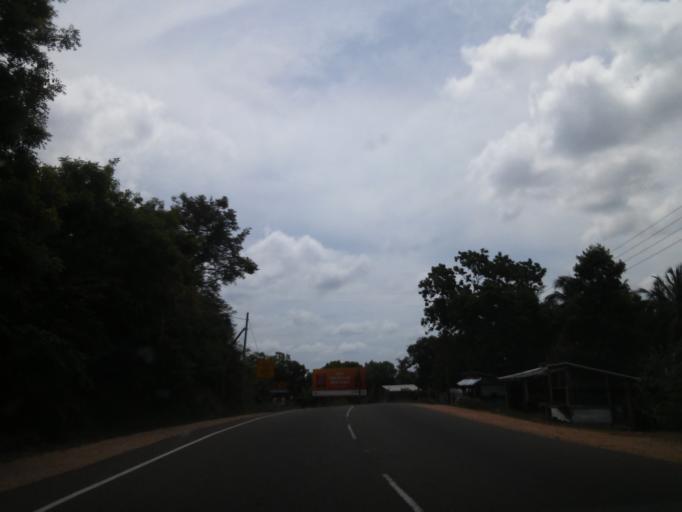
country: LK
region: Eastern Province
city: Trincomalee
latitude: 8.3495
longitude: 80.9842
